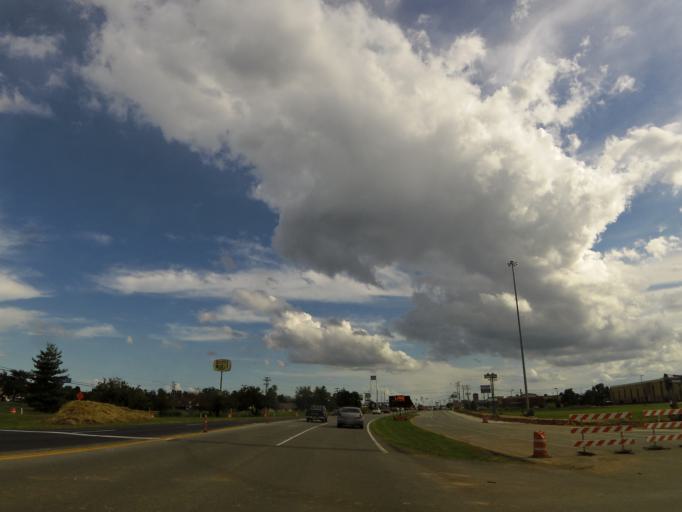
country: US
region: Kentucky
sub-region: Christian County
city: Hopkinsville
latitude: 36.8305
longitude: -87.4728
